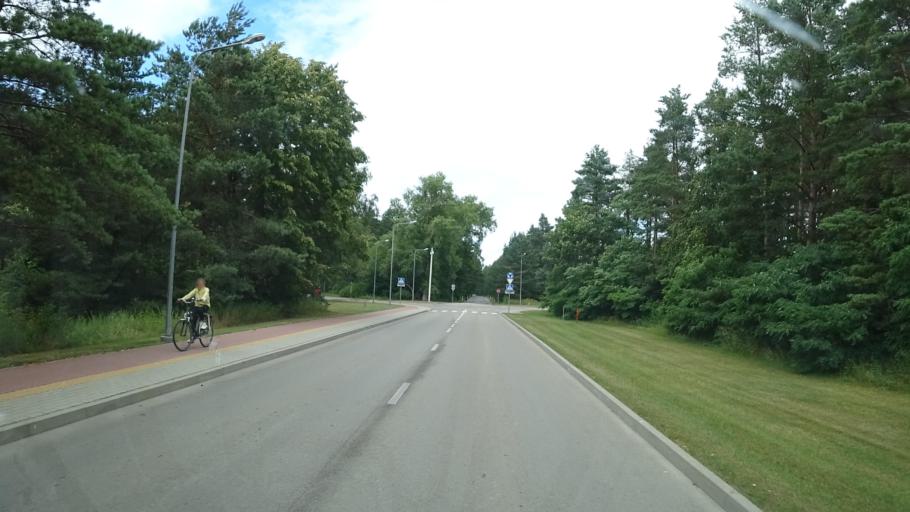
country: LT
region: Klaipedos apskritis
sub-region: Klaipeda
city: Palanga
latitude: 55.9374
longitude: 21.0791
